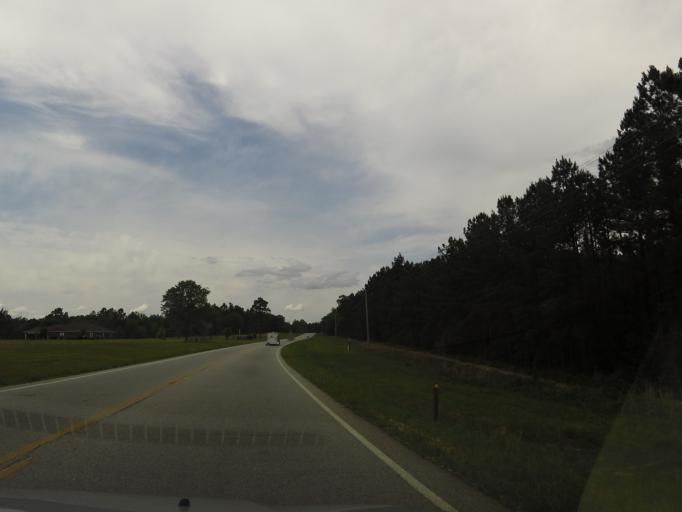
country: US
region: Georgia
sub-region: Emanuel County
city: Swainsboro
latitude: 32.5055
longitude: -82.2597
